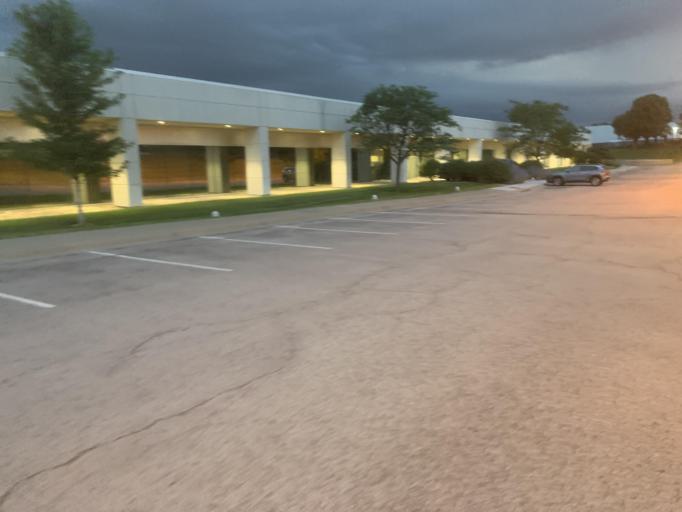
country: US
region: Nebraska
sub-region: Douglas County
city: Ralston
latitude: 41.1884
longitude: -96.0839
